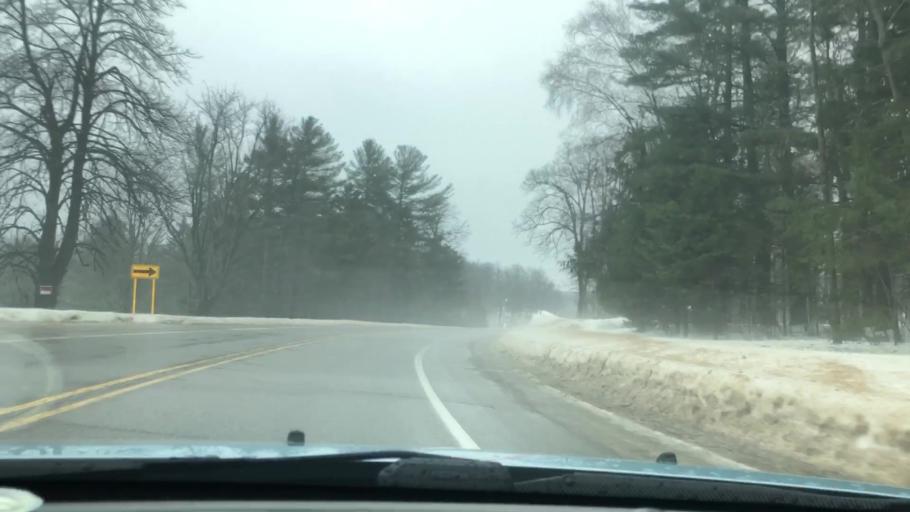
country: US
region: Michigan
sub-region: Otsego County
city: Gaylord
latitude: 45.0612
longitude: -84.7850
